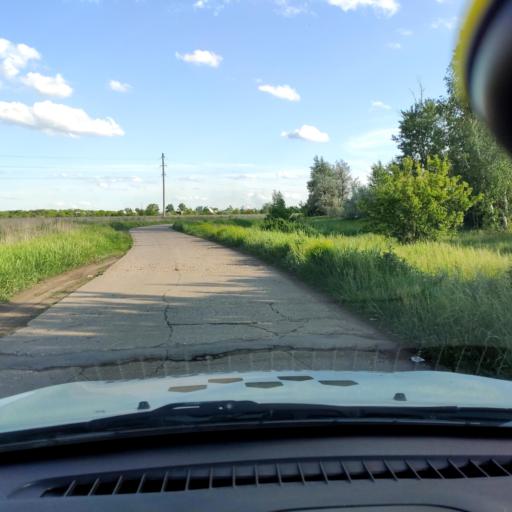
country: RU
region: Samara
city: Tol'yatti
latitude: 53.5965
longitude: 49.4570
